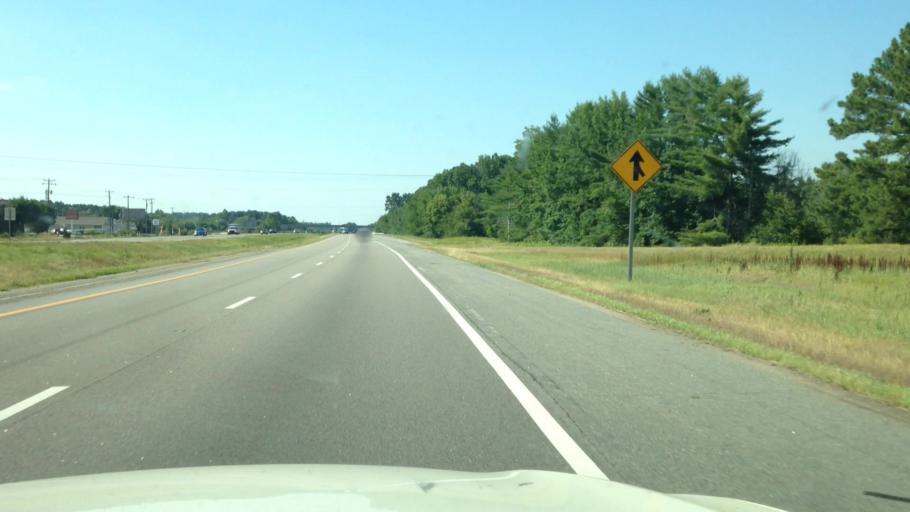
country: US
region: Virginia
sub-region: Sussex County
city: Sussex
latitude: 36.9452
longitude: -77.3920
